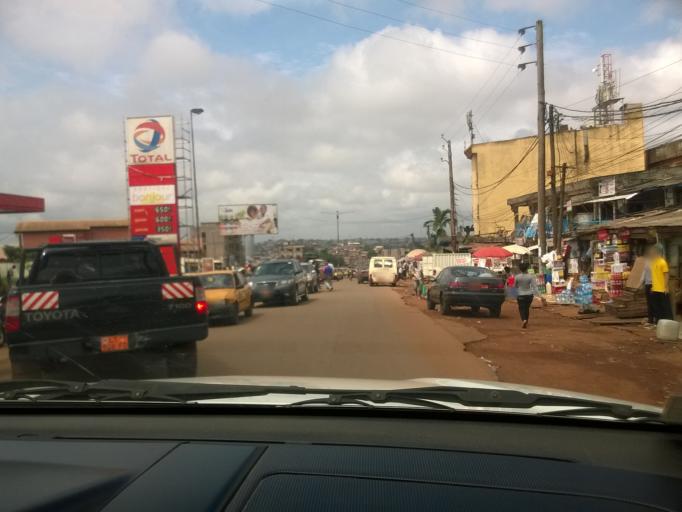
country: CM
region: Centre
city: Yaounde
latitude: 3.8679
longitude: 11.5495
